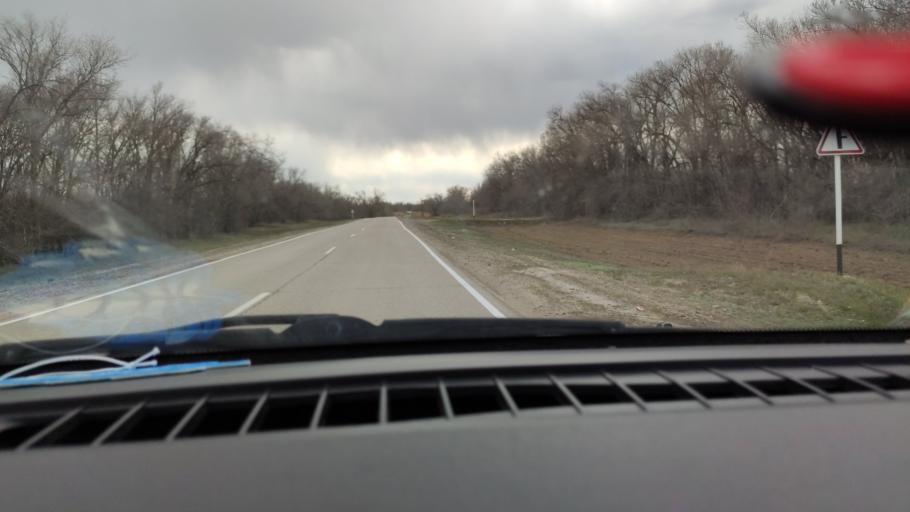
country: RU
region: Saratov
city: Privolzhskiy
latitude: 51.2382
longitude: 45.9259
